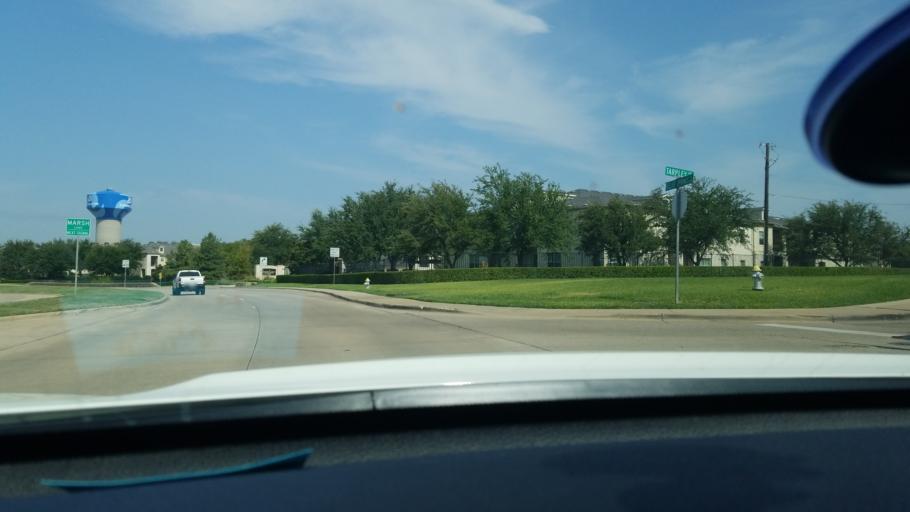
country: US
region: Texas
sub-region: Dallas County
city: Addison
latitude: 32.9706
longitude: -96.8516
